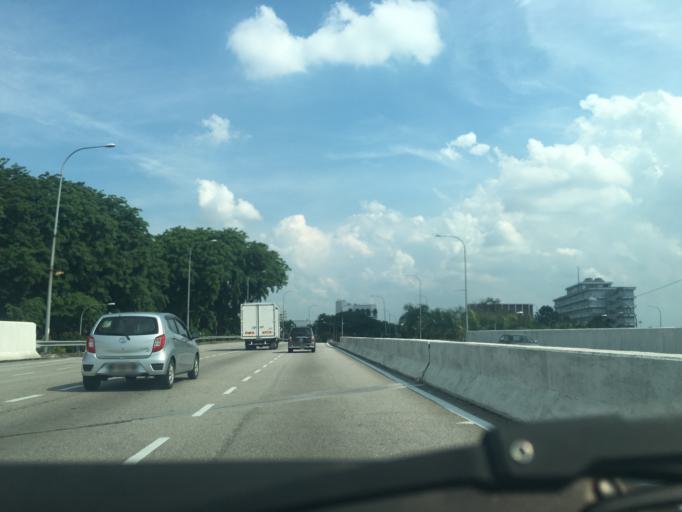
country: MY
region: Perak
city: Ipoh
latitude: 4.6091
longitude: 101.0784
